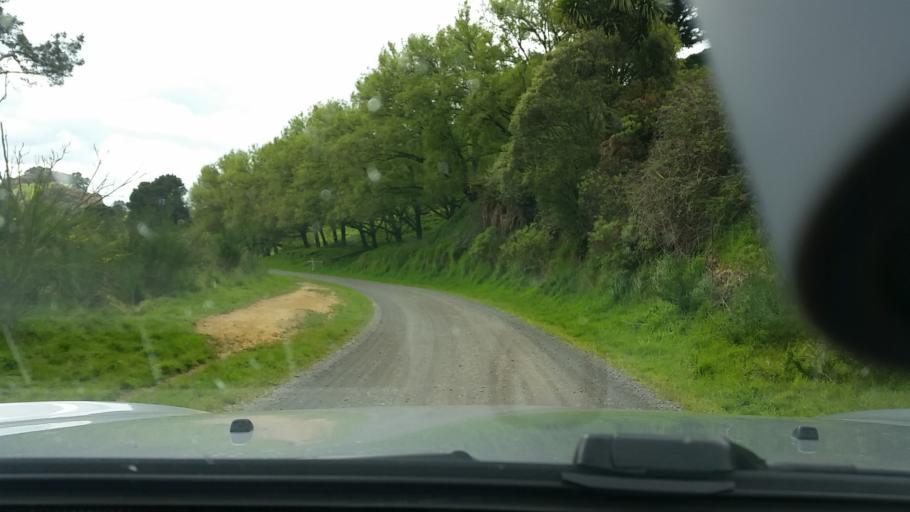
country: NZ
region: Waikato
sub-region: Taupo District
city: Taupo
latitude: -38.4650
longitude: 176.2418
